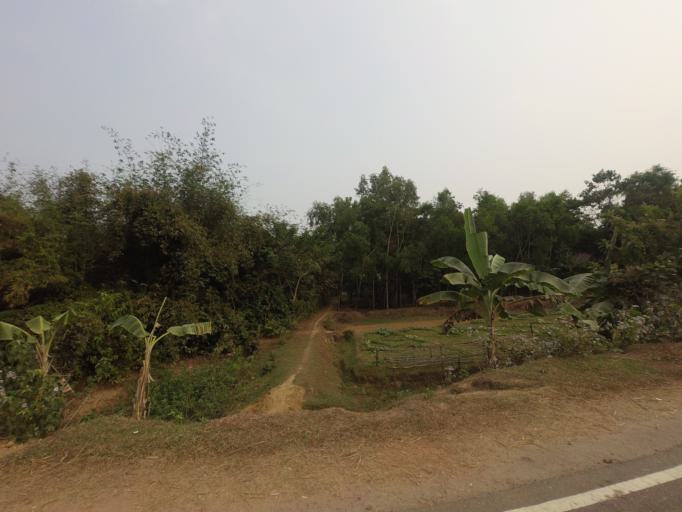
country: BD
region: Dhaka
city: Netrakona
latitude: 25.1667
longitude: 90.6585
